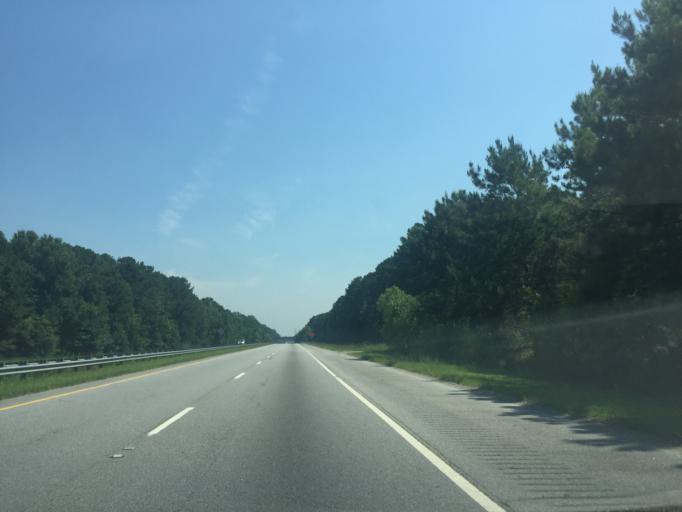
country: US
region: Georgia
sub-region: Chatham County
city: Georgetown
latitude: 32.0217
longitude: -81.1724
